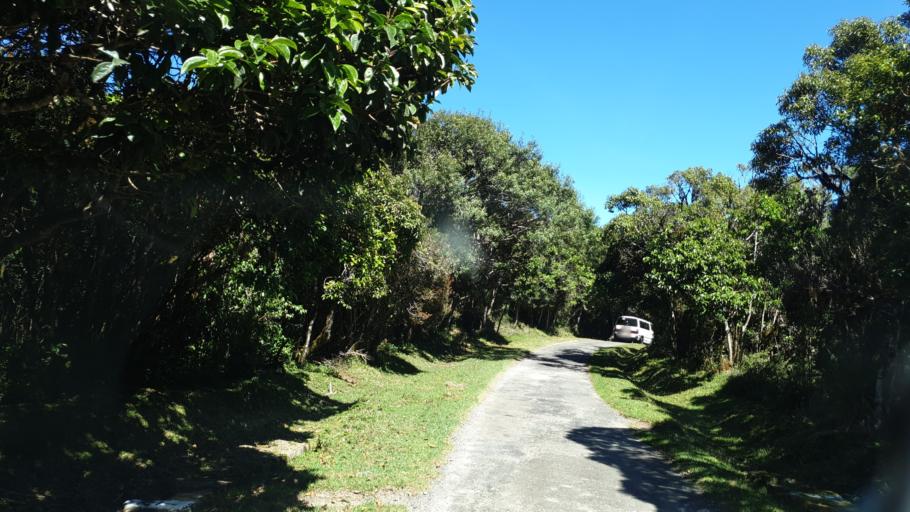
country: LK
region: Uva
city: Haputale
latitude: 6.8034
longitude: 80.8327
